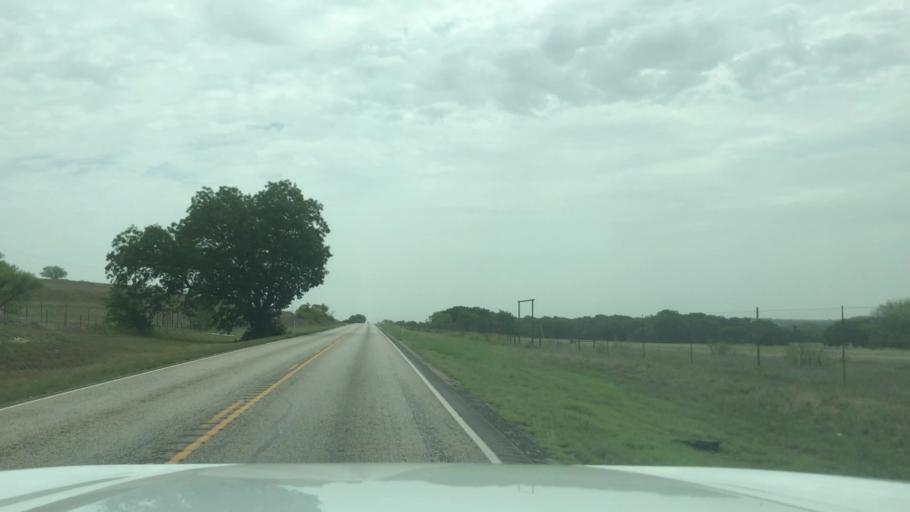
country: US
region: Texas
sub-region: Erath County
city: Dublin
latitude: 32.0569
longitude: -98.1853
